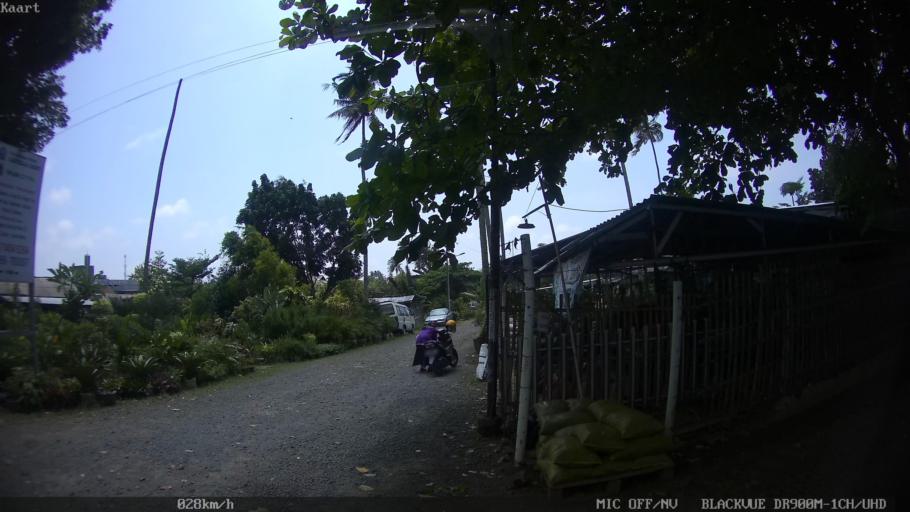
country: ID
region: Lampung
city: Kedaton
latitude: -5.3751
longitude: 105.2661
